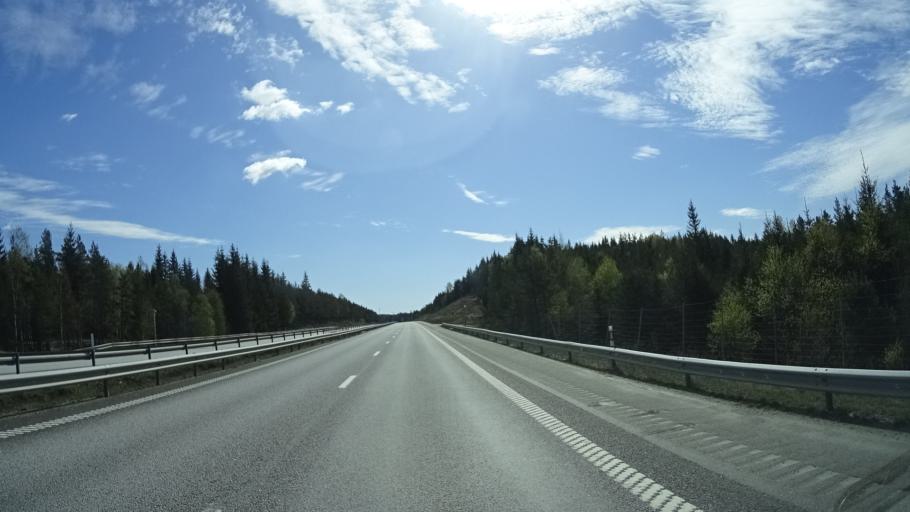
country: SE
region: Vaestra Goetaland
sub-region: Harryda Kommun
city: Hindas
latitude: 57.6711
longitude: 12.3697
